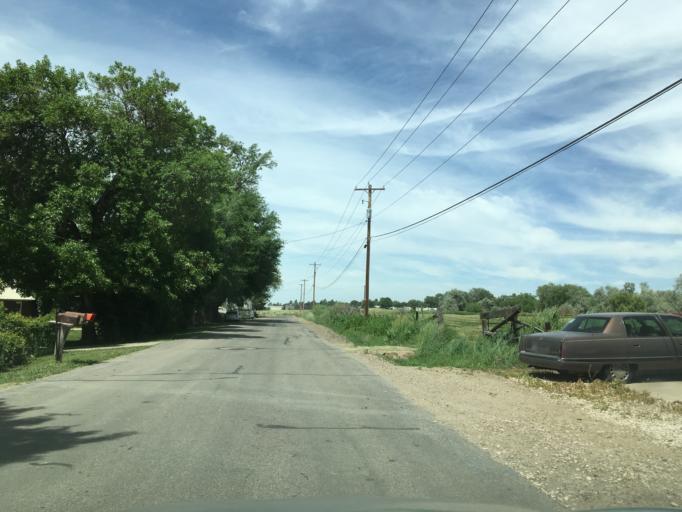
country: US
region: Utah
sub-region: Davis County
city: Hill Air Force Bace
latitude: 41.0988
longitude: -111.9575
